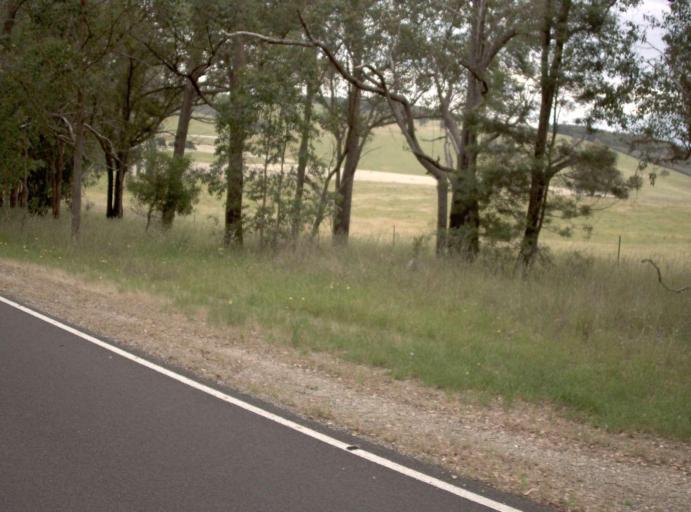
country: AU
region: Victoria
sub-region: East Gippsland
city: Bairnsdale
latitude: -37.7396
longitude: 147.3130
